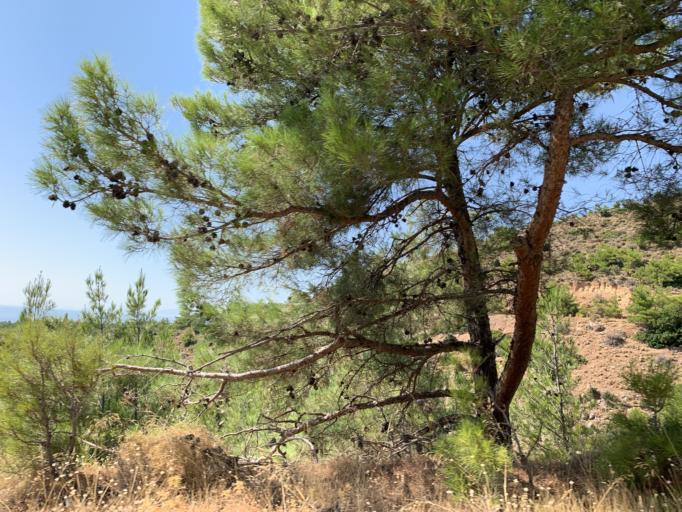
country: GR
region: North Aegean
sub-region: Chios
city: Vrontados
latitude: 38.4082
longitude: 25.9745
